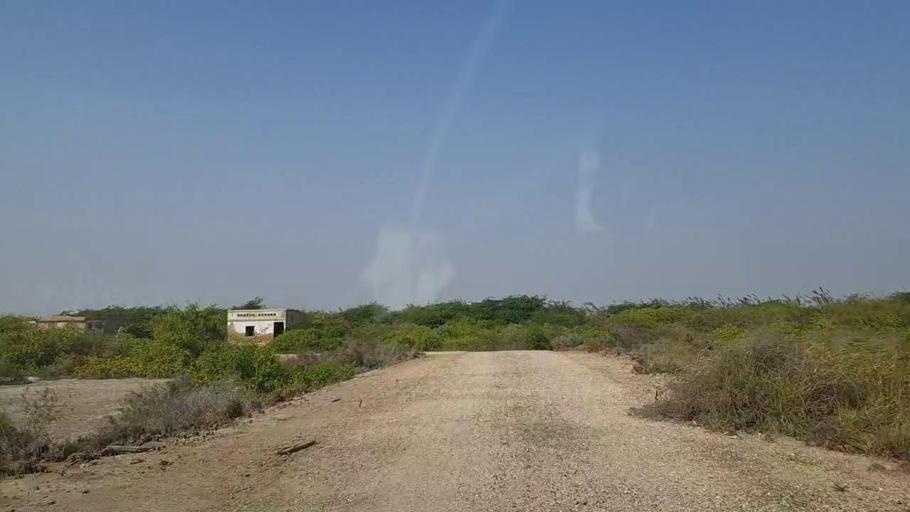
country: PK
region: Sindh
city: Mirpur Sakro
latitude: 24.6610
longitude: 67.7261
